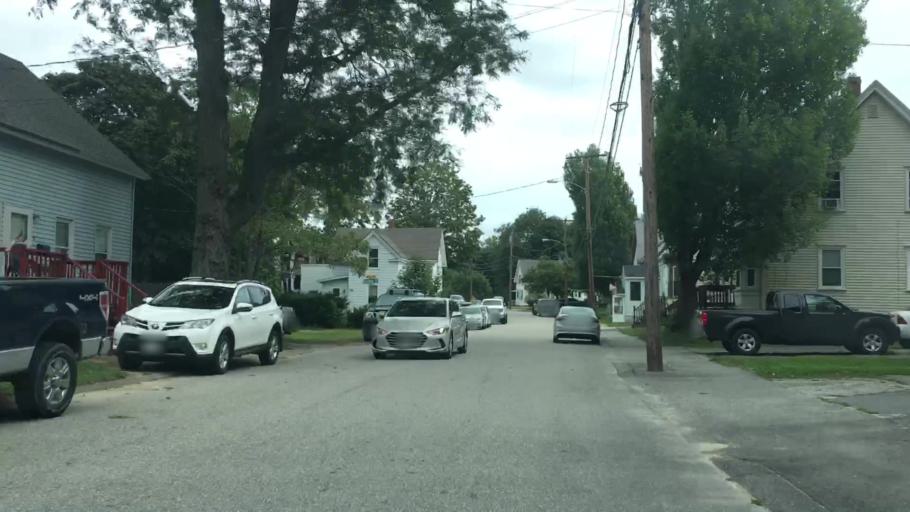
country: US
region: Maine
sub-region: Cumberland County
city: Westbrook
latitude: 43.6726
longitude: -70.3665
